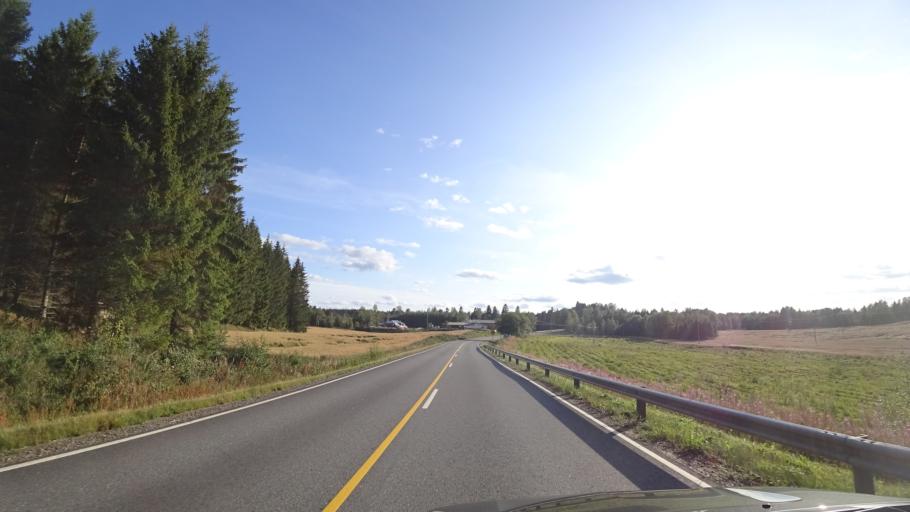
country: FI
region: Paijanne Tavastia
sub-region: Lahti
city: Hollola
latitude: 61.1427
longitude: 25.3310
